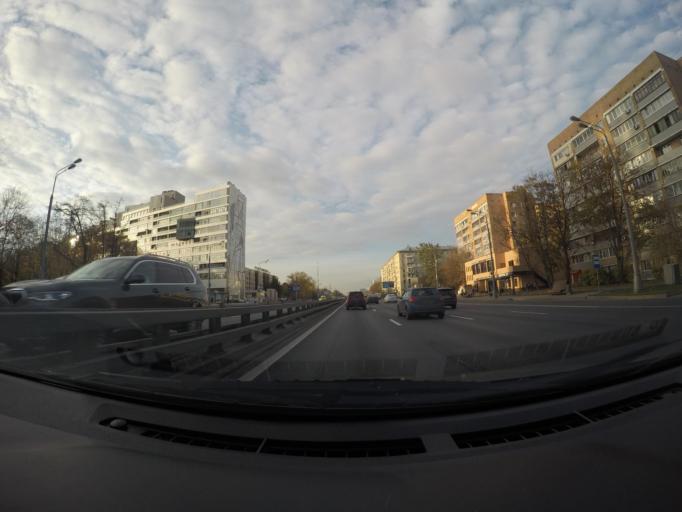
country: RU
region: Moskovskaya
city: Levoberezhnyy
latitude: 55.8315
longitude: 37.4876
